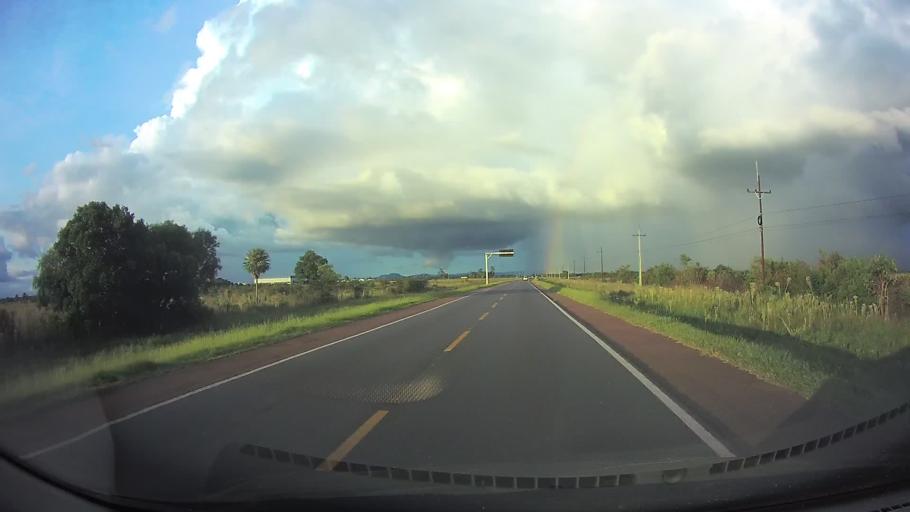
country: PY
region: Paraguari
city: Carapegua
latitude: -25.7436
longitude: -57.2134
